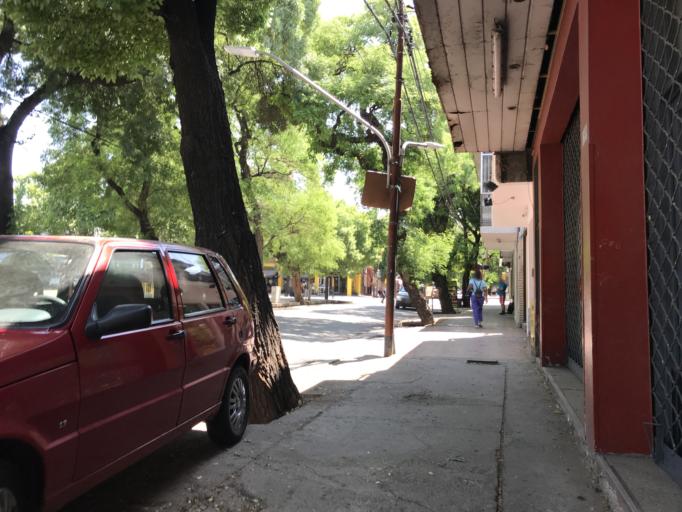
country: AR
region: Mendoza
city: Mendoza
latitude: -32.8911
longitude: -68.8336
